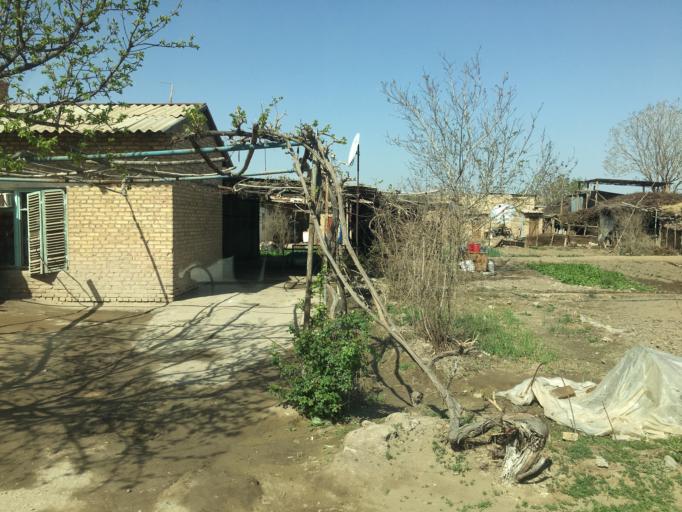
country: TM
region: Lebap
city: Turkmenabat
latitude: 38.9611
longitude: 63.6496
